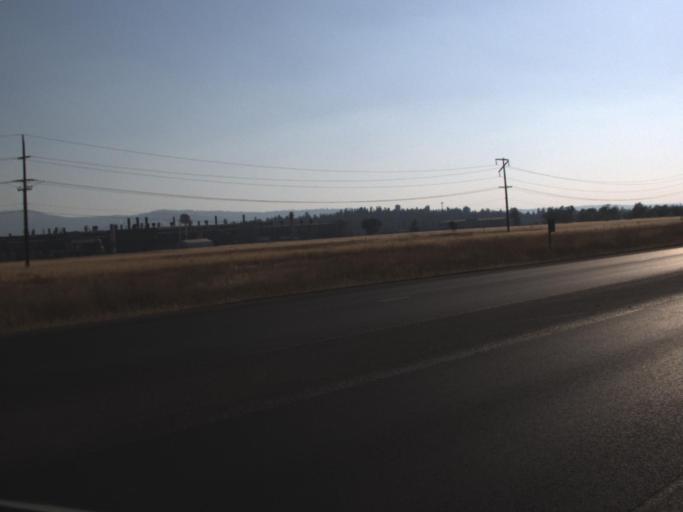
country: US
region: Washington
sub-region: Spokane County
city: Trentwood
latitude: 47.6950
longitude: -117.2085
